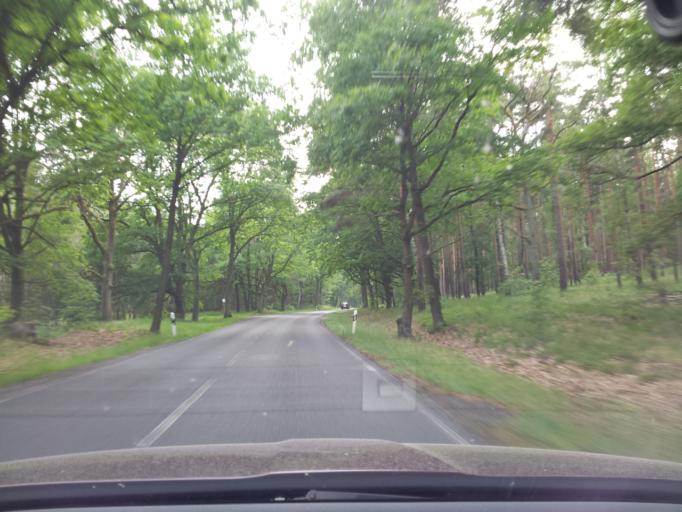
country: DE
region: Brandenburg
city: Beelitz
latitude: 52.3016
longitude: 12.9577
